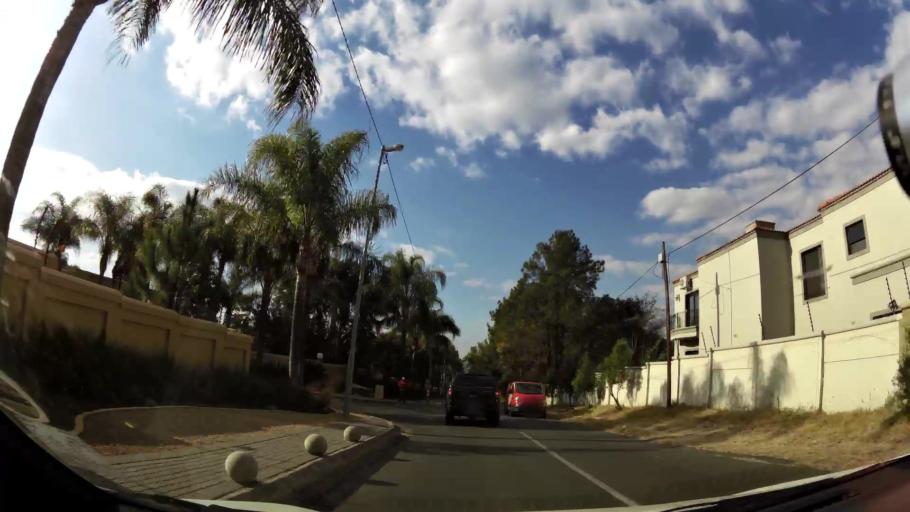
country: ZA
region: Gauteng
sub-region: City of Johannesburg Metropolitan Municipality
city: Diepsloot
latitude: -26.0065
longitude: 28.0191
